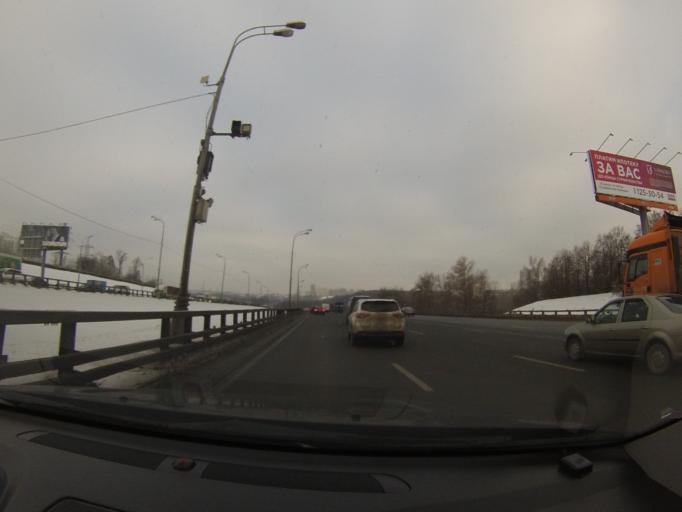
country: RU
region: Moscow
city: Strogino
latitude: 55.8379
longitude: 37.3966
